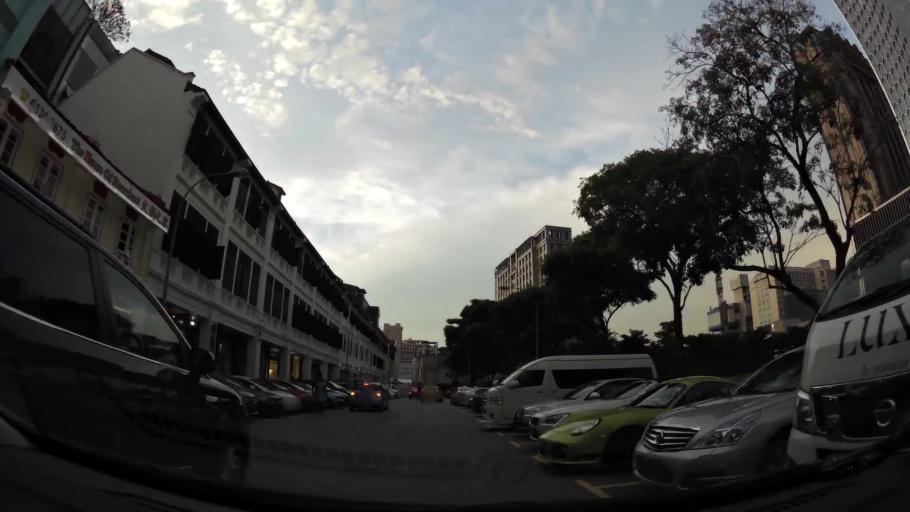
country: SG
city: Singapore
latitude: 1.2983
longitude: 103.8570
